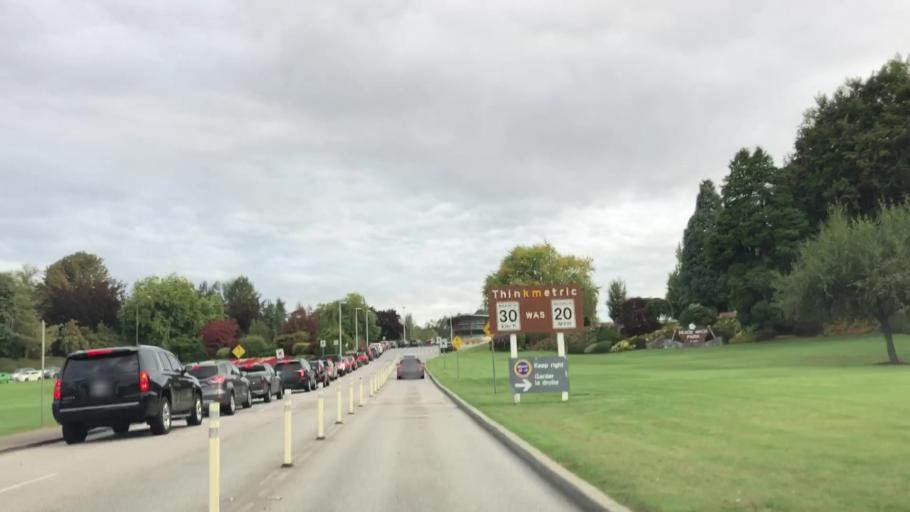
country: US
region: Washington
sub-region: Whatcom County
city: Blaine
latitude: 49.0024
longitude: -122.7562
